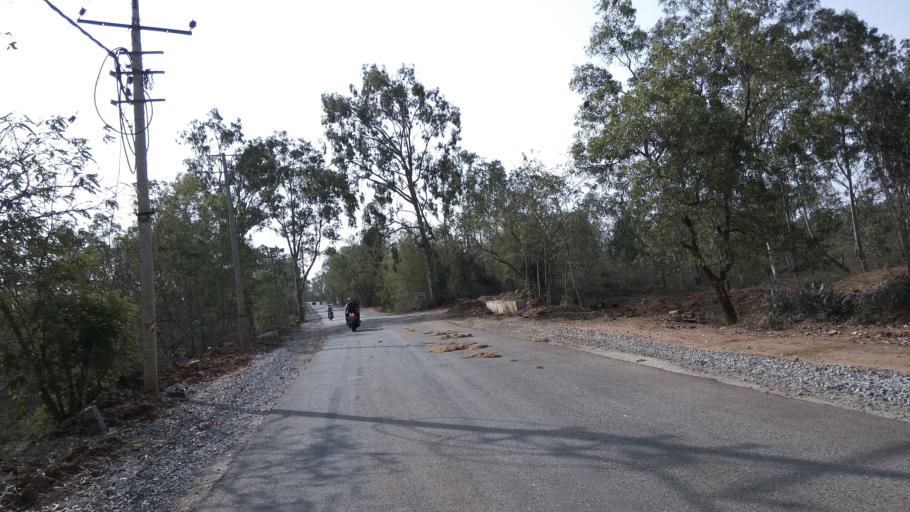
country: IN
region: Karnataka
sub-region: Kolar
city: Bangarapet
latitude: 13.0858
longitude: 78.2166
